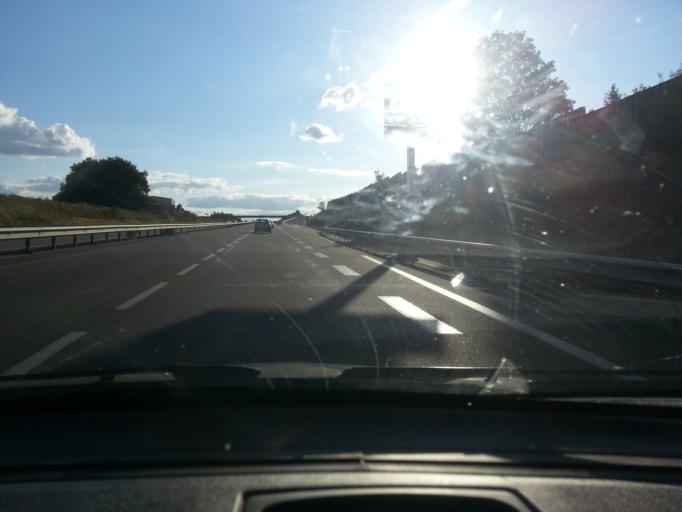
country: FR
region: Bourgogne
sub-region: Departement de Saone-et-Loire
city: Buxy
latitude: 46.7541
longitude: 4.6766
